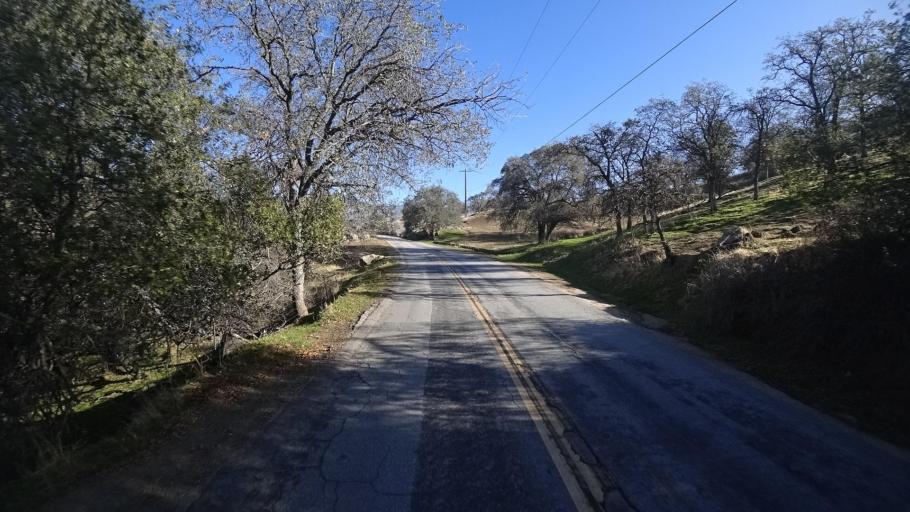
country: US
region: California
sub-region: Kern County
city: Alta Sierra
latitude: 35.7210
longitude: -118.8113
